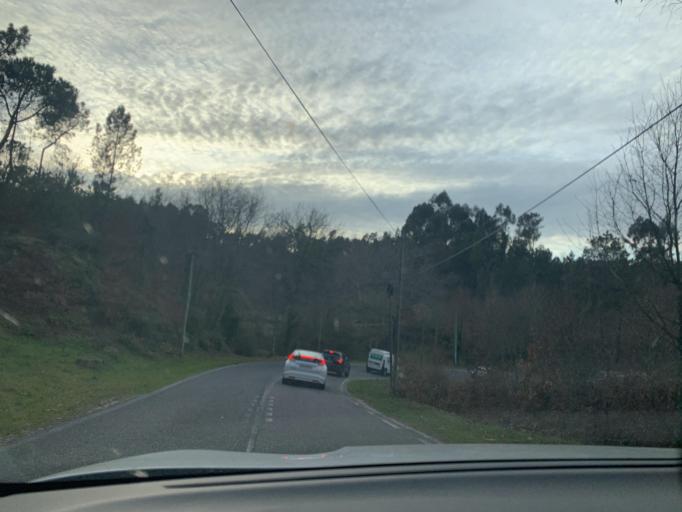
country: PT
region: Viseu
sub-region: Viseu
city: Viseu
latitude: 40.5998
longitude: -7.9929
